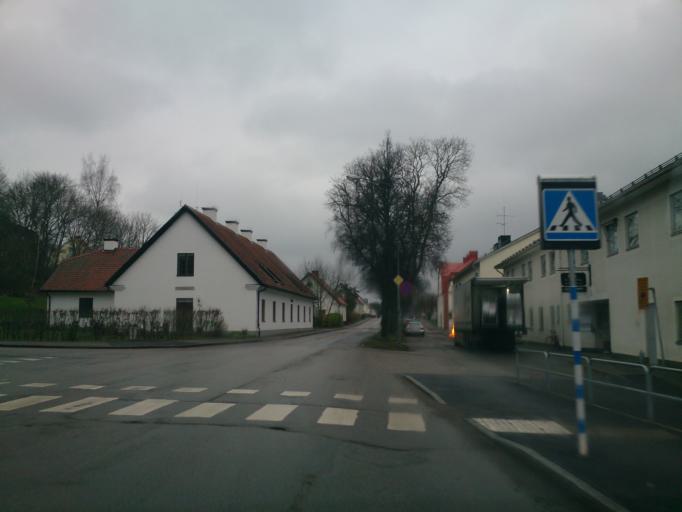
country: SE
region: OEstergoetland
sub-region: Atvidabergs Kommun
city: Atvidaberg
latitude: 58.2007
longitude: 15.9979
